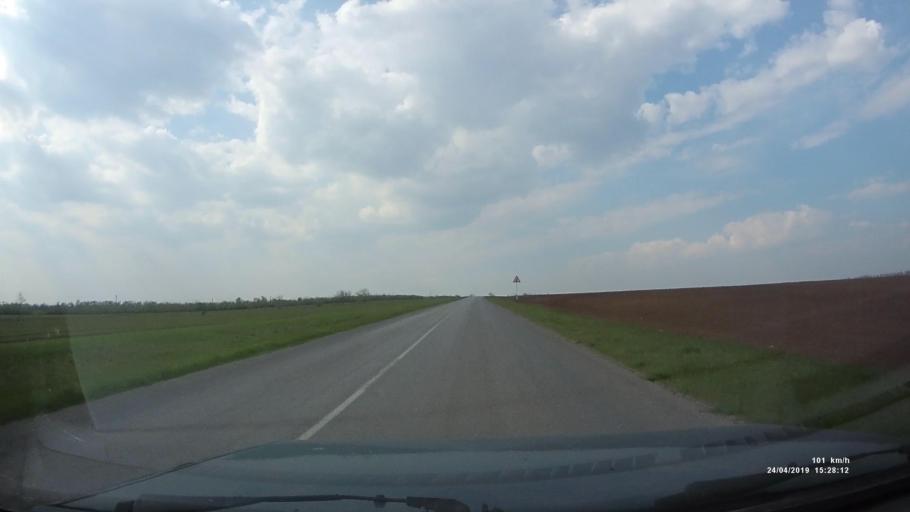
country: RU
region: Rostov
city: Remontnoye
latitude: 46.5757
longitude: 43.0200
